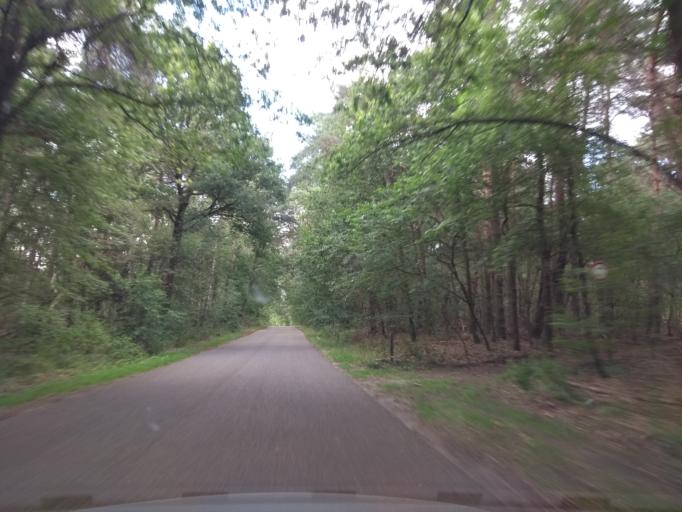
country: NL
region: Overijssel
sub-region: Gemeente Hof van Twente
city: Markelo
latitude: 52.2735
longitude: 6.4768
